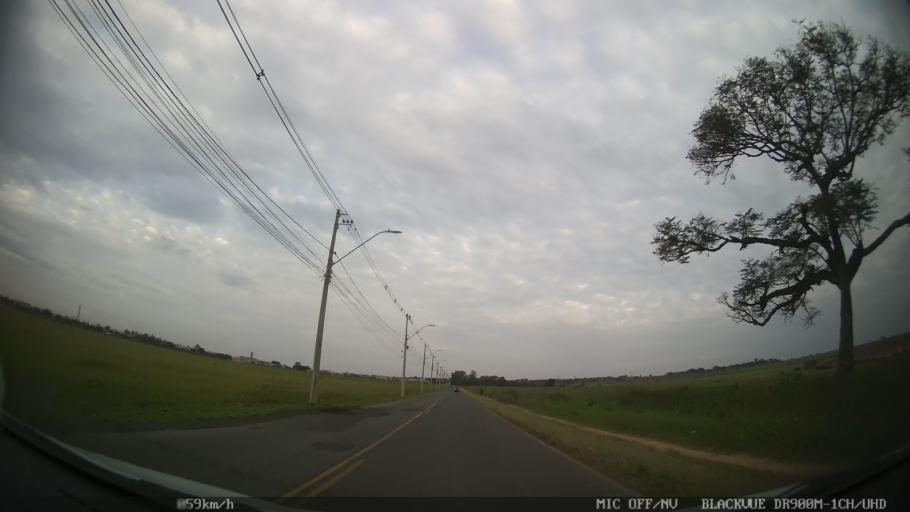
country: BR
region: Sao Paulo
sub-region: Americana
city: Americana
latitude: -22.7053
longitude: -47.3780
